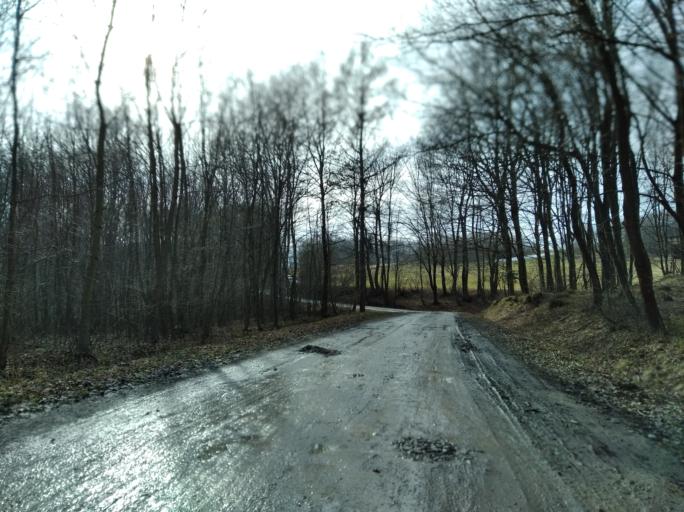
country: PL
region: Subcarpathian Voivodeship
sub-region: Powiat brzozowski
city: Gorki
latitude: 49.6419
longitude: 22.0635
